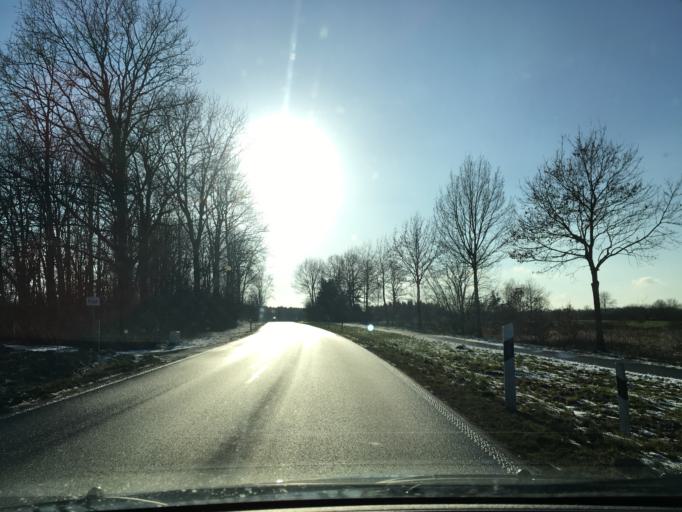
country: DE
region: Schleswig-Holstein
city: Krukow
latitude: 53.4364
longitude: 10.4741
